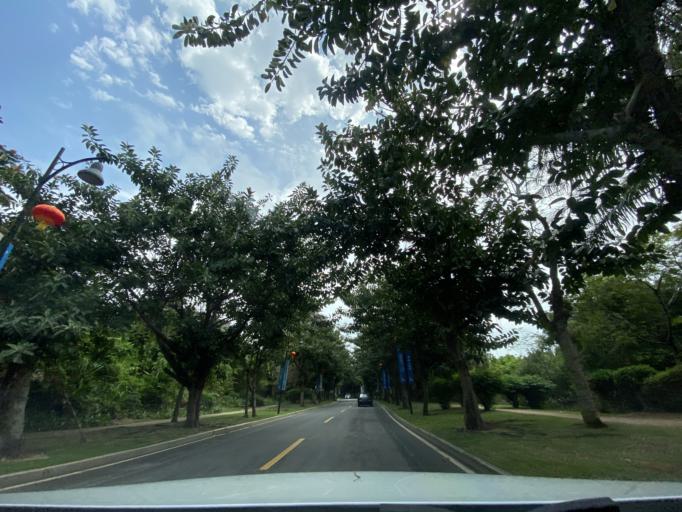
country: CN
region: Hainan
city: Liji
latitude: 18.6695
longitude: 110.2699
